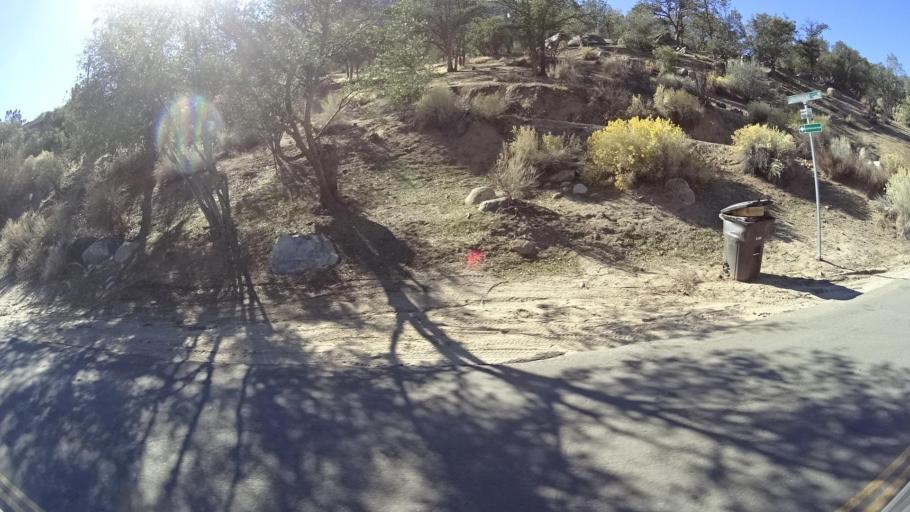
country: US
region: California
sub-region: Kern County
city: Kernville
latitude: 35.7744
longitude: -118.4433
